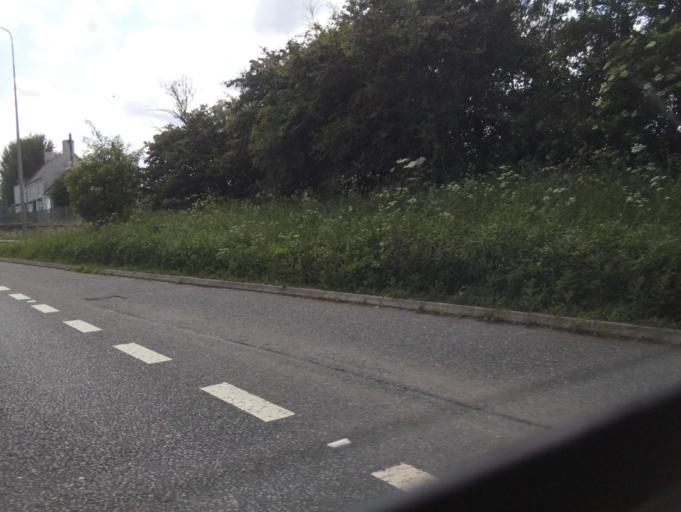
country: GB
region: England
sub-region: Hartlepool
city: Elwick
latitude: 54.6676
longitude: -1.3002
